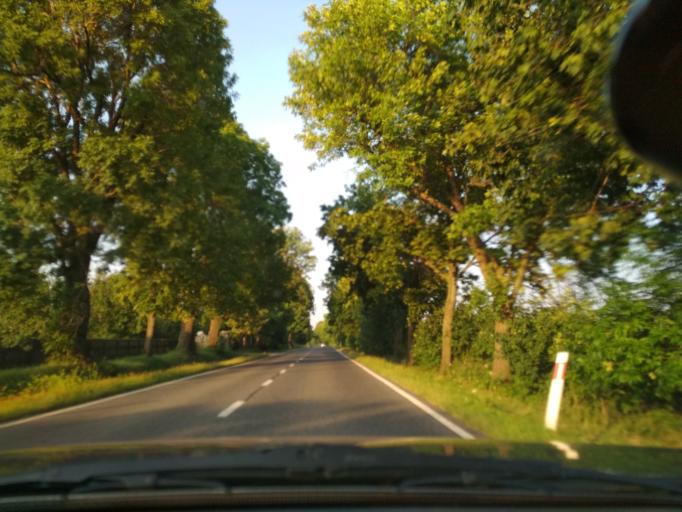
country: PL
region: Silesian Voivodeship
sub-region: Powiat zawiercianski
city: Pilica
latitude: 50.4674
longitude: 19.6164
